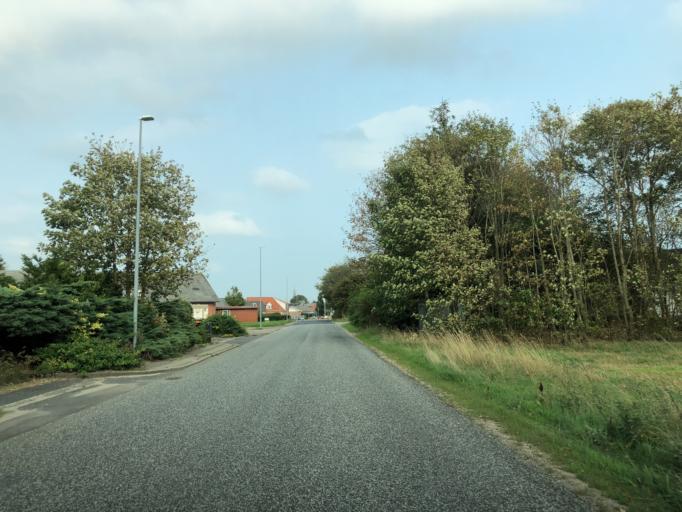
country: DK
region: Central Jutland
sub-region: Herning Kommune
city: Kibaek
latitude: 55.9906
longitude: 8.7400
